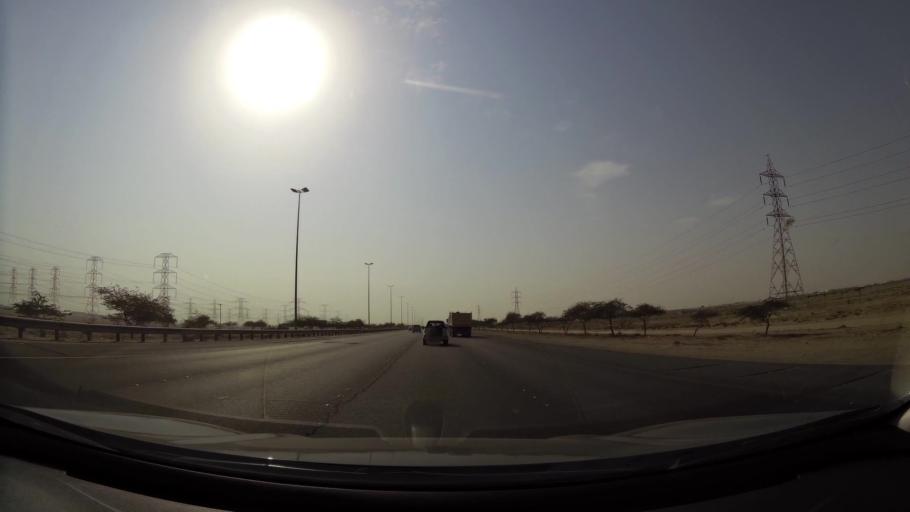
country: KW
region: Al Ahmadi
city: Al Ahmadi
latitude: 28.9795
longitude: 48.1082
